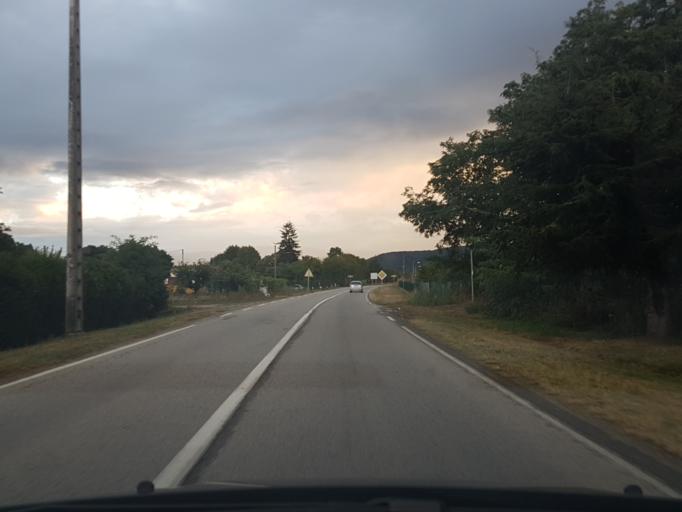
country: FR
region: Midi-Pyrenees
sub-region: Departement de l'Ariege
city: Verniolle
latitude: 43.0784
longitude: 1.6513
